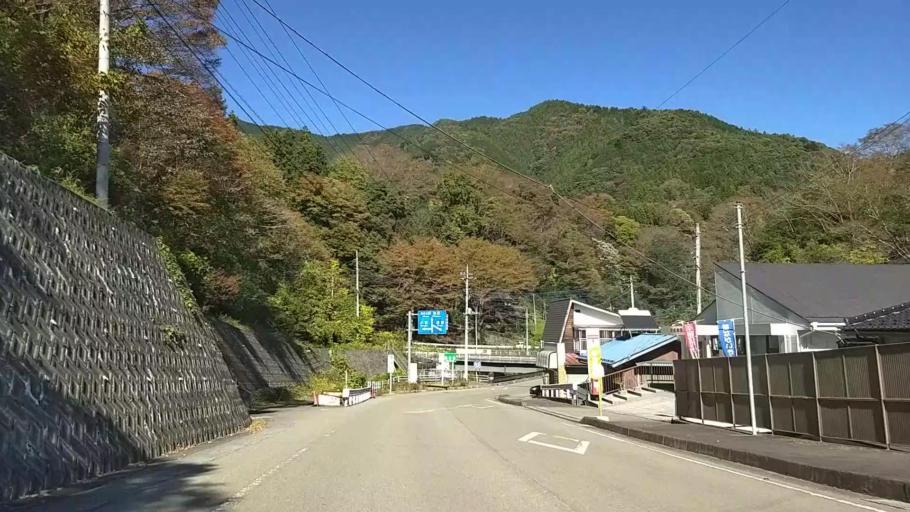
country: JP
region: Yamanashi
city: Uenohara
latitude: 35.6721
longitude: 139.0894
